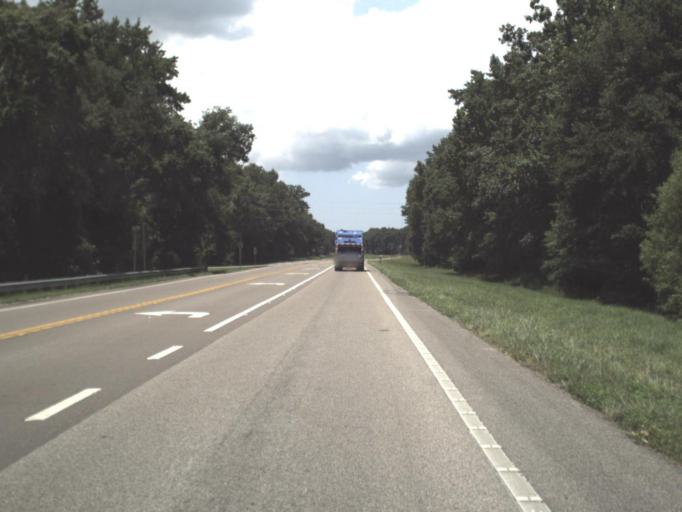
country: US
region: Florida
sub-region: Hernando County
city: North Brooksville
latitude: 28.6149
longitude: -82.4070
